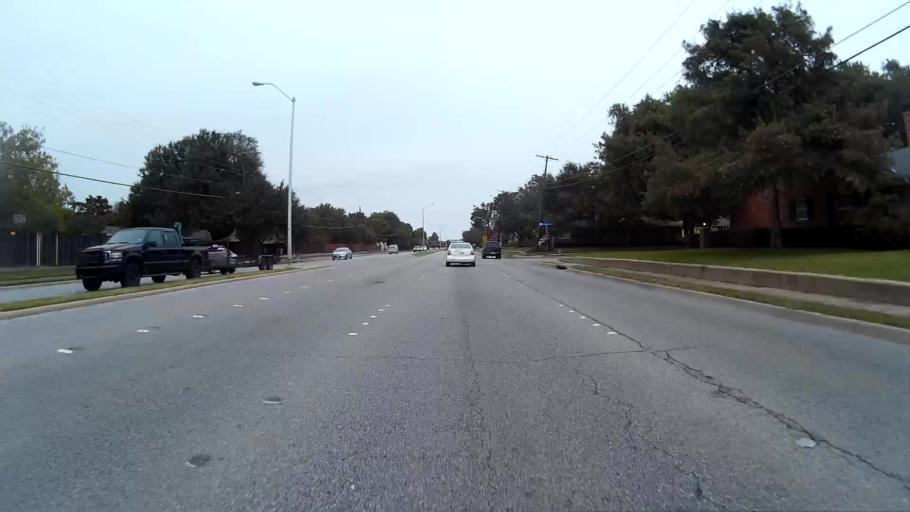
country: US
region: Texas
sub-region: Dallas County
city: Richardson
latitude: 32.9677
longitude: -96.7688
